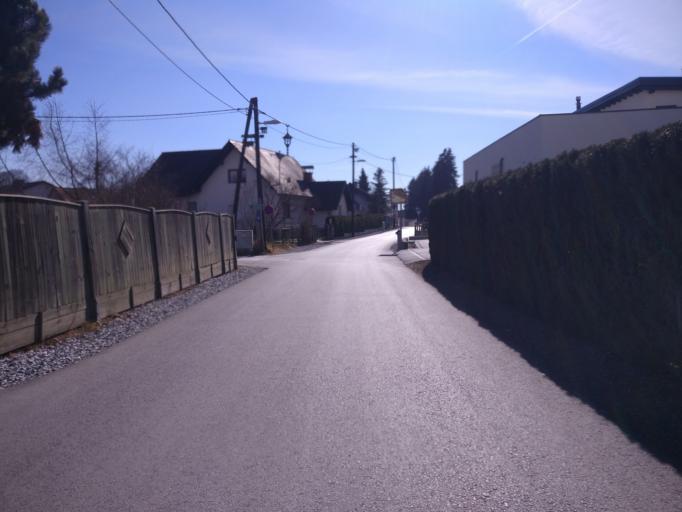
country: AT
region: Styria
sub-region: Politischer Bezirk Graz-Umgebung
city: Feldkirchen bei Graz
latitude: 47.0147
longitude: 15.4480
